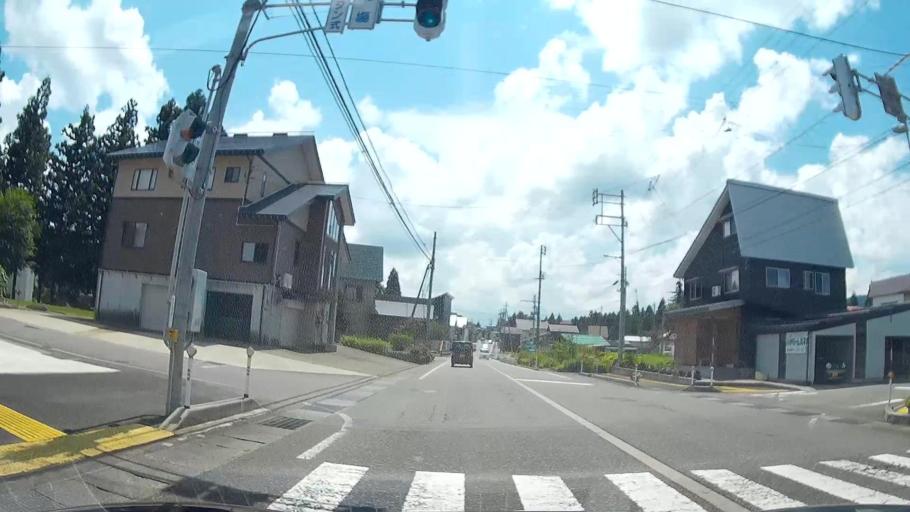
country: JP
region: Niigata
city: Tokamachi
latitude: 37.0786
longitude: 138.7188
